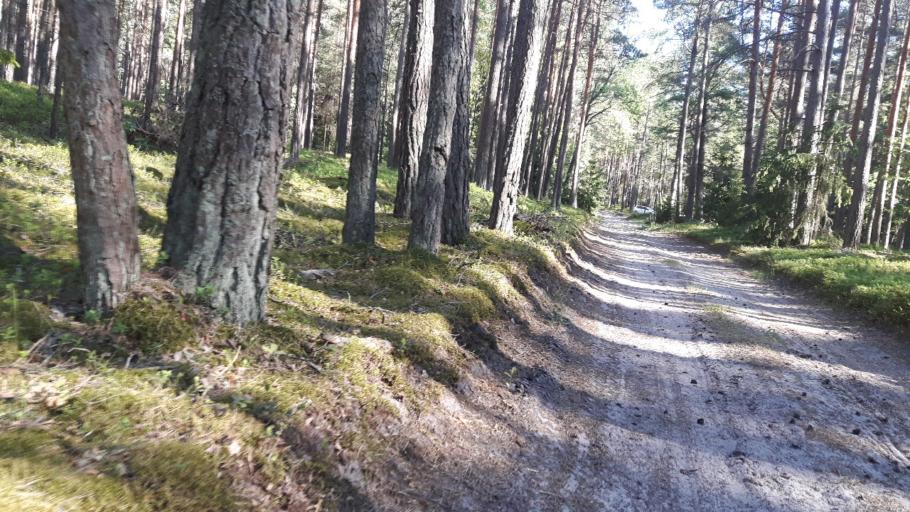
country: LV
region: Salacgrivas
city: Salacgriva
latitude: 57.7107
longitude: 24.3517
